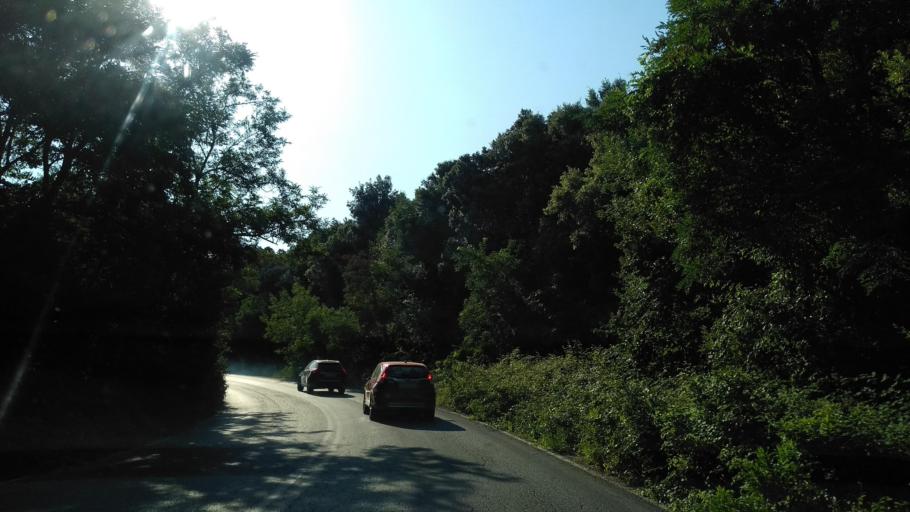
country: GR
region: Central Macedonia
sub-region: Nomos Thessalonikis
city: Stavros
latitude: 40.6553
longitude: 23.7373
